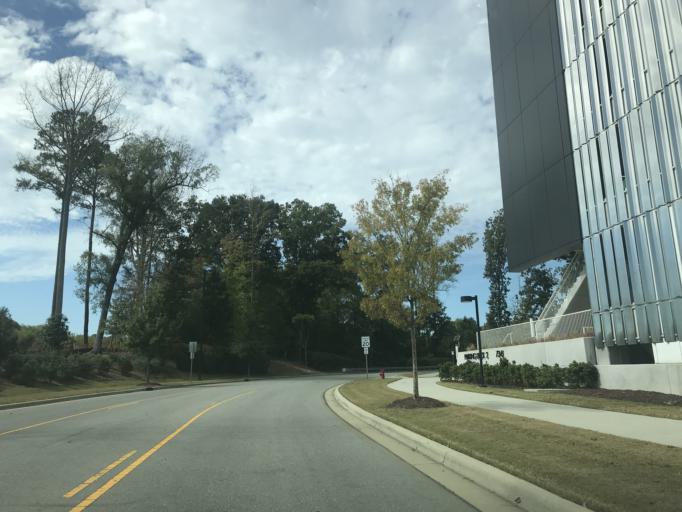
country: US
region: North Carolina
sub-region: Wake County
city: Knightdale
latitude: 35.8654
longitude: -78.5413
